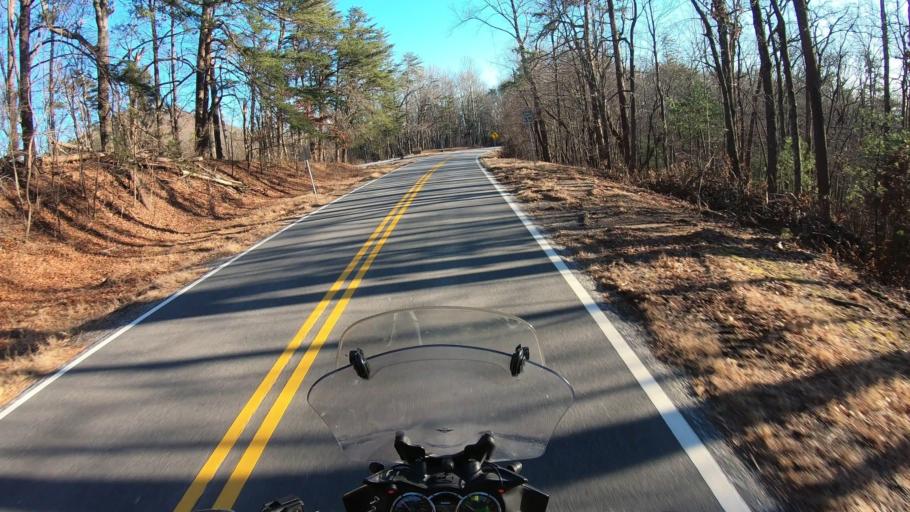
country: US
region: Georgia
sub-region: Lumpkin County
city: Dahlonega
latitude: 34.6654
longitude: -83.9826
